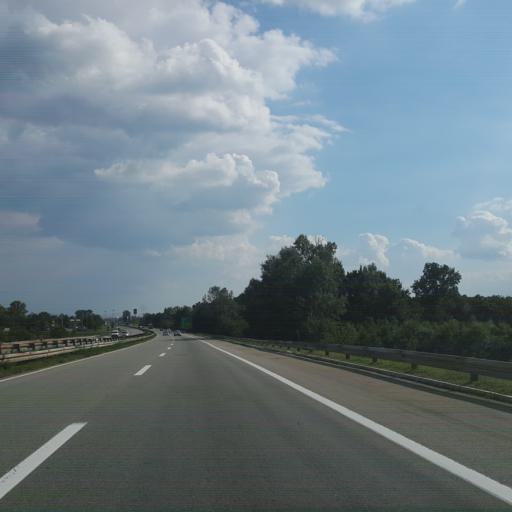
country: RS
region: Central Serbia
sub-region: Podunavski Okrug
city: Velika Plana
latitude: 44.3534
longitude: 21.0731
